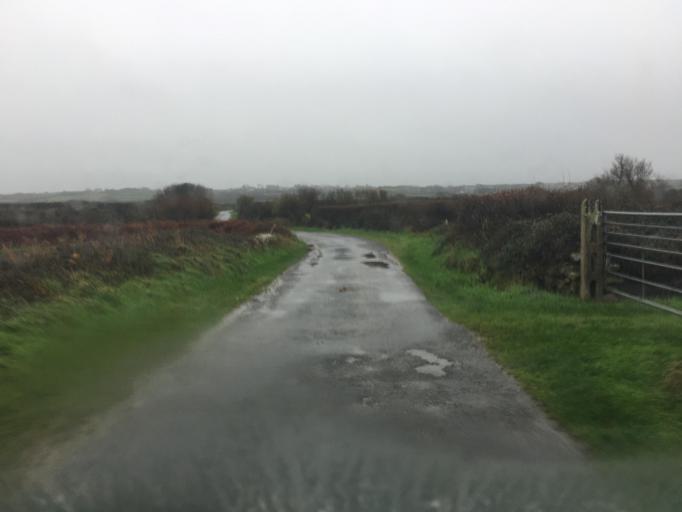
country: FR
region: Lower Normandy
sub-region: Departement de la Manche
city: Beaumont-Hague
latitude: 49.7210
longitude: -1.9215
